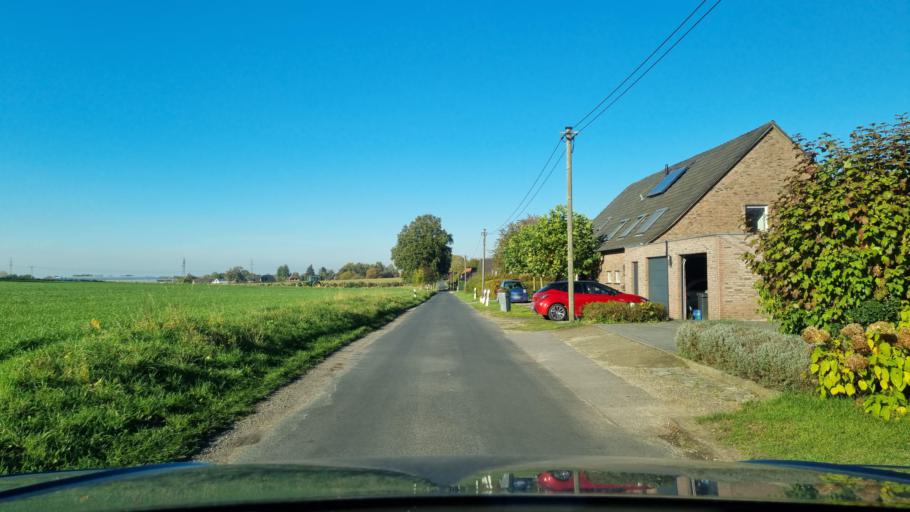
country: DE
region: North Rhine-Westphalia
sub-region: Regierungsbezirk Dusseldorf
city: Kranenburg
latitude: 51.7783
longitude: 6.0631
